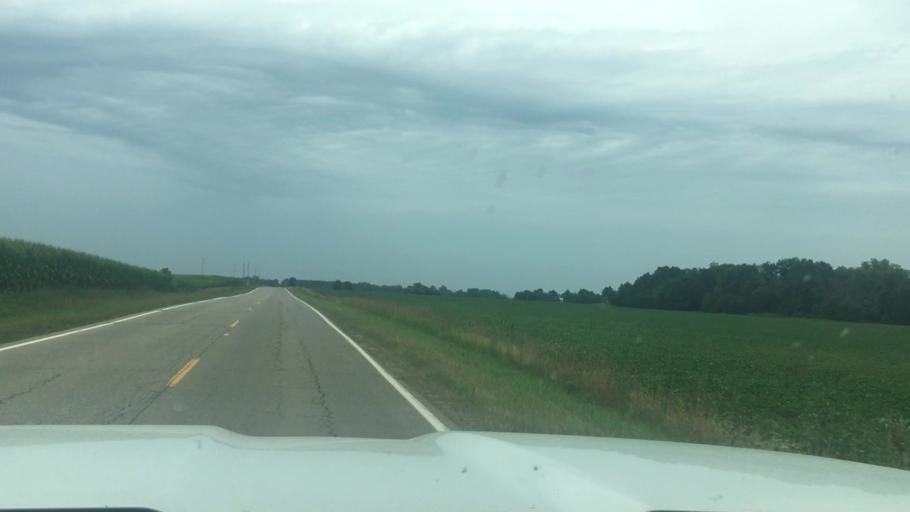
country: US
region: Michigan
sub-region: Clinton County
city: Saint Johns
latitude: 43.0256
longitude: -84.4843
